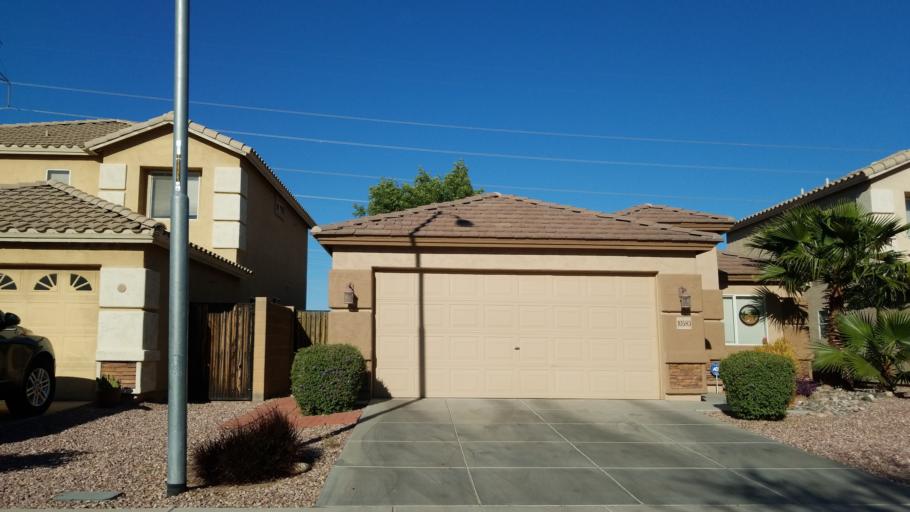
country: US
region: Arizona
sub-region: Maricopa County
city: Youngtown
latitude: 33.5792
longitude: -112.3085
